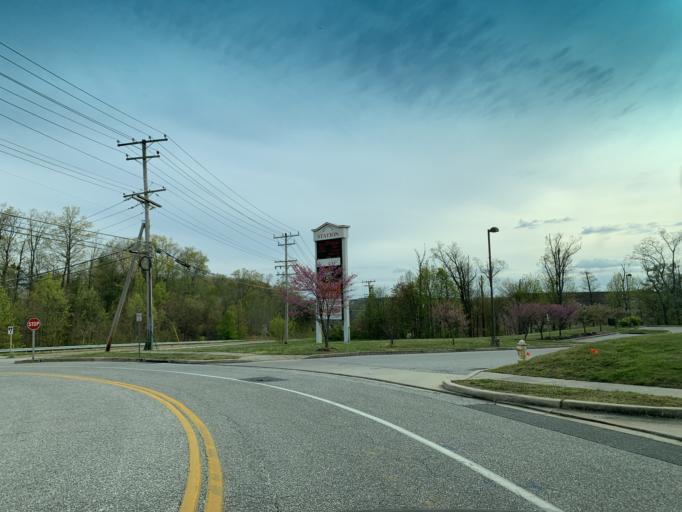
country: US
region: Maryland
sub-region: Harford County
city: Riverside
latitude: 39.4811
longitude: -76.2541
